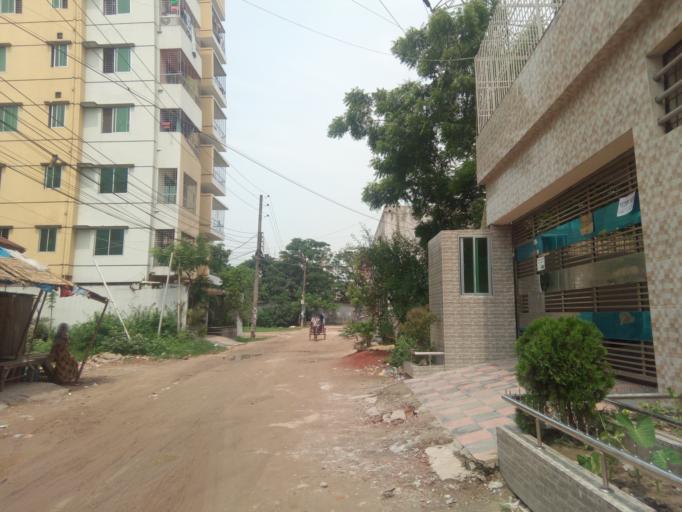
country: BD
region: Dhaka
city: Paltan
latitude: 23.7607
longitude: 90.4396
